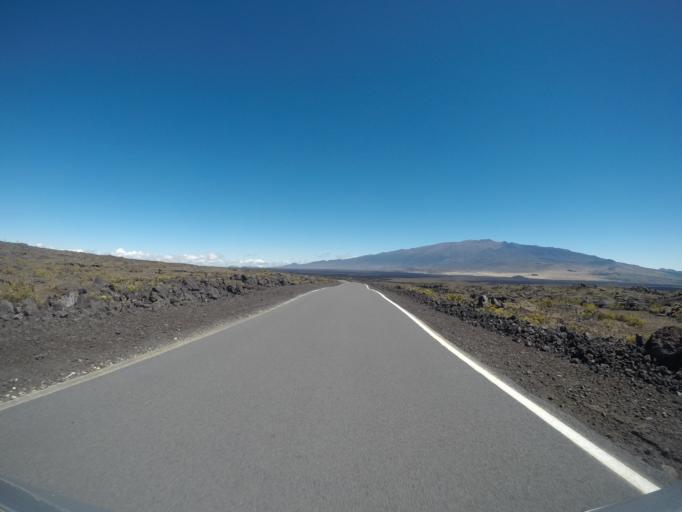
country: US
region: Hawaii
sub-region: Hawaii County
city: Volcano
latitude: 19.6237
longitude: -155.4753
